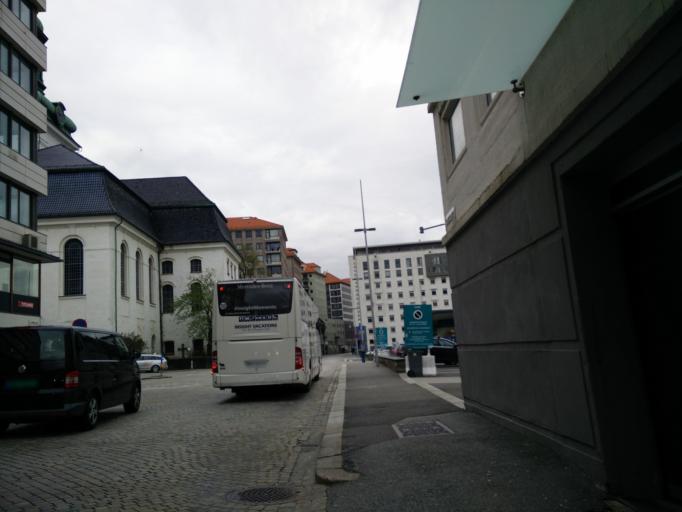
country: NO
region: Hordaland
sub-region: Bergen
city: Bergen
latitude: 60.3969
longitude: 5.3148
